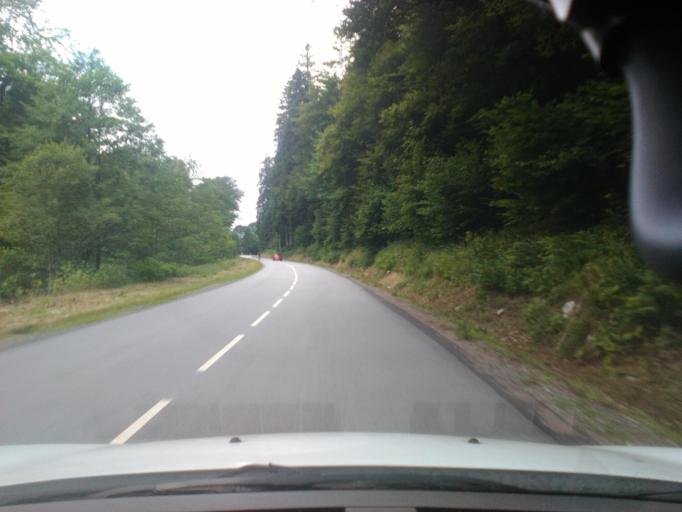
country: FR
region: Lorraine
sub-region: Departement des Vosges
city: Gerardmer
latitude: 48.1105
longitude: 6.8572
